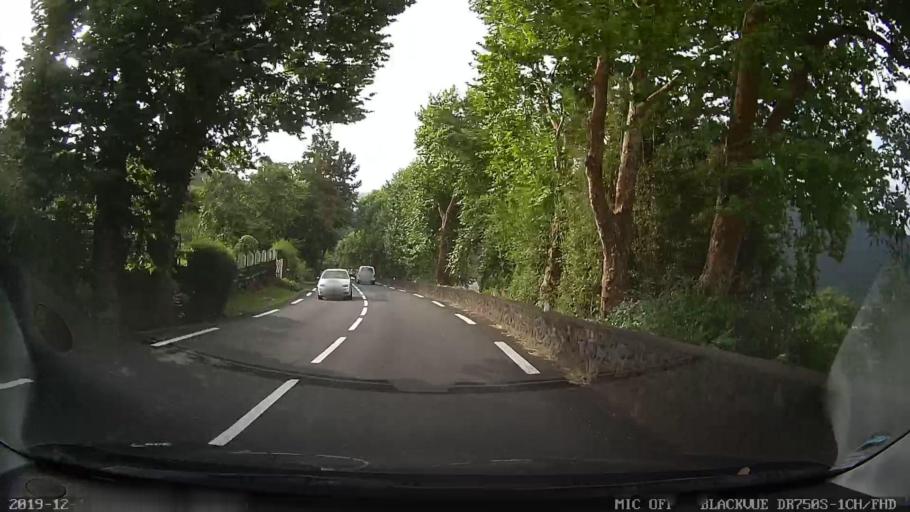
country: RE
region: Reunion
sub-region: Reunion
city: Cilaos
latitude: -21.1515
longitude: 55.6158
